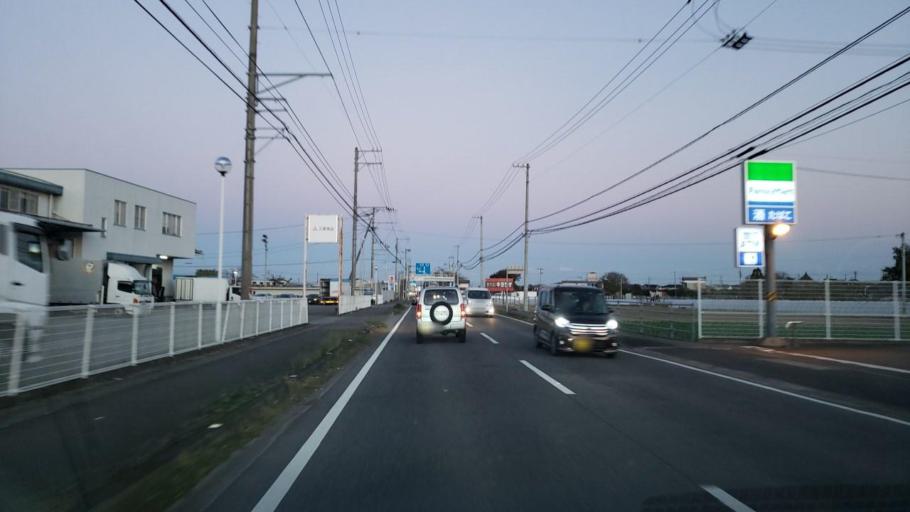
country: JP
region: Tokushima
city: Ishii
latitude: 34.1227
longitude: 134.4552
